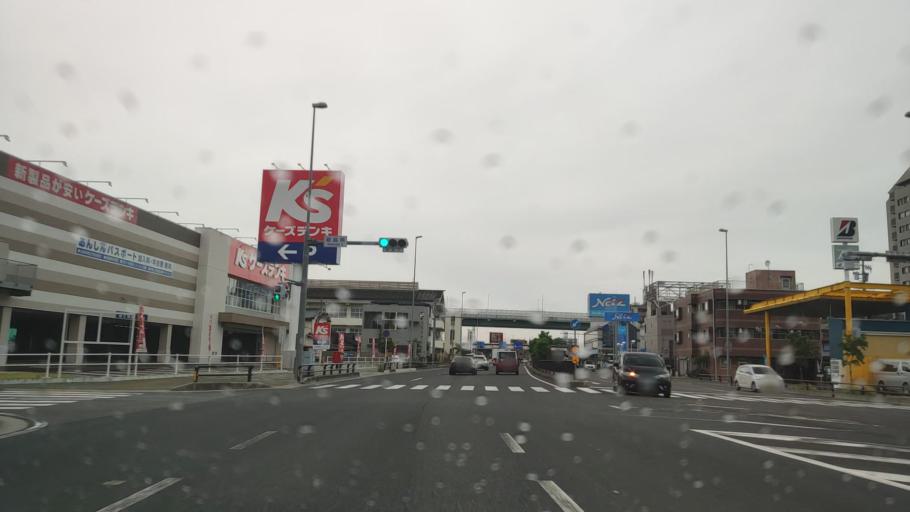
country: JP
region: Aichi
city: Nagoya-shi
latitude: 35.2006
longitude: 136.8813
